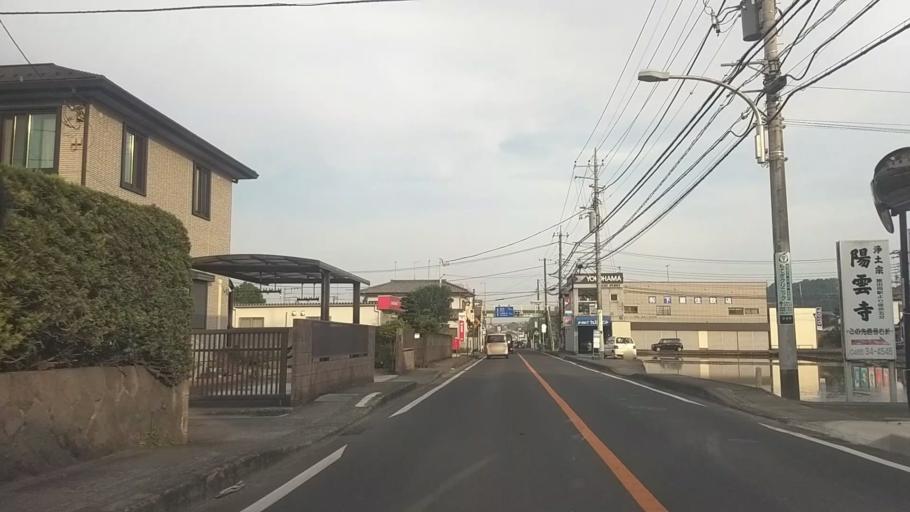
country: JP
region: Kanagawa
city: Odawara
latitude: 35.2885
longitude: 139.1375
